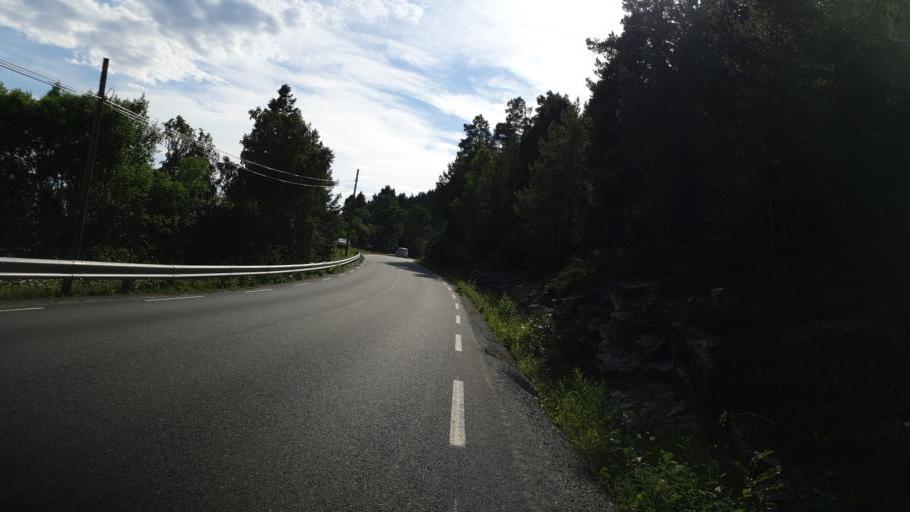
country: NO
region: Sor-Trondelag
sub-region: Trondheim
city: Trondheim
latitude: 63.5630
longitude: 10.3259
